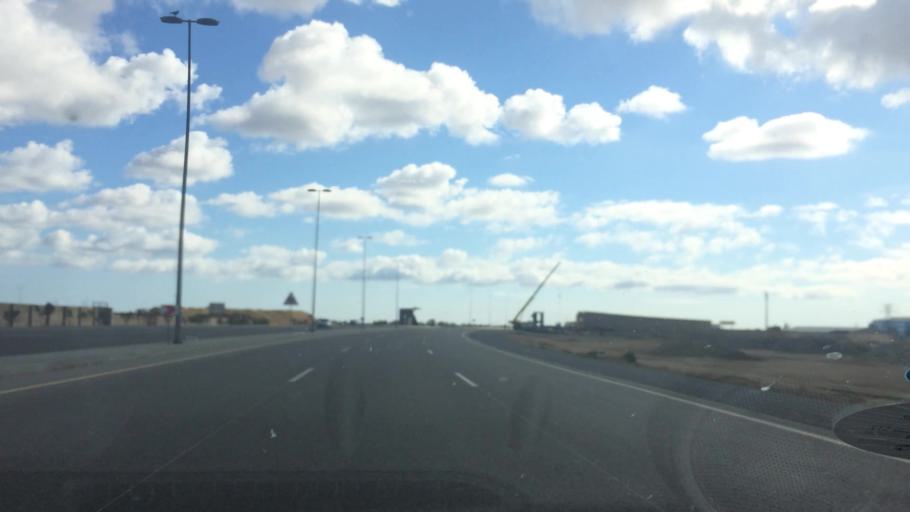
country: AZ
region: Baki
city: Qala
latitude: 40.4576
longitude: 50.1386
